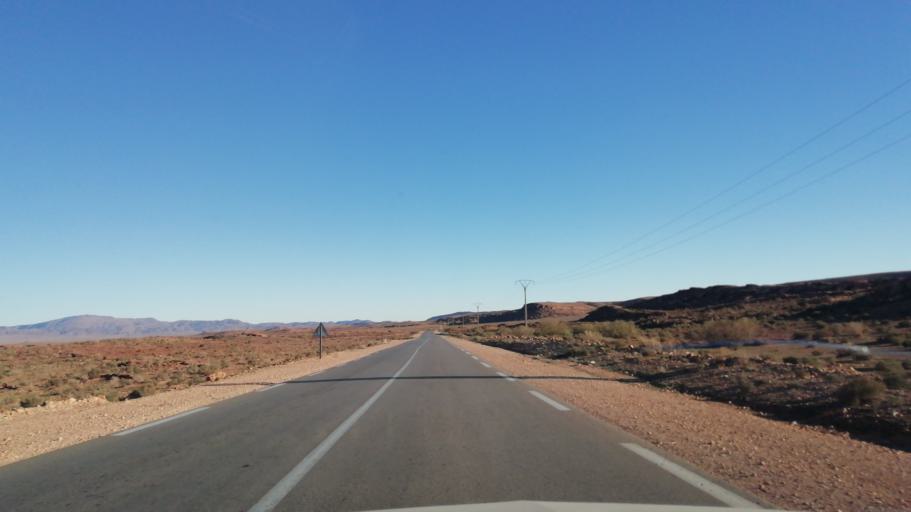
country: DZ
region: El Bayadh
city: El Abiodh Sidi Cheikh
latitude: 33.1720
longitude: 0.4561
